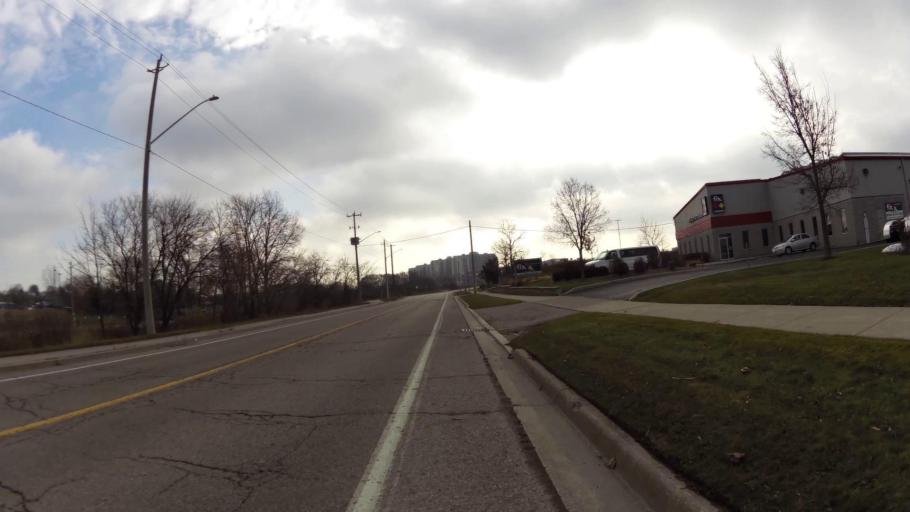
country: CA
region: Ontario
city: Kitchener
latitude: 43.4245
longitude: -80.4706
